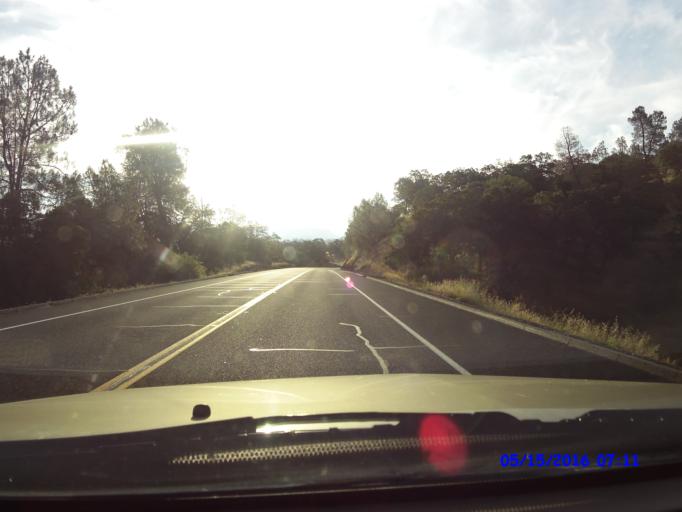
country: US
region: California
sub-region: Tuolumne County
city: Jamestown
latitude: 37.8504
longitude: -120.3967
